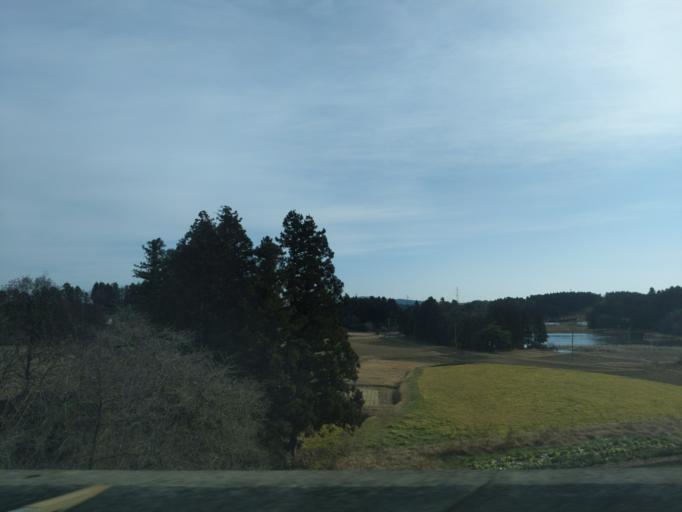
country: JP
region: Miyagi
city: Furukawa
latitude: 38.6354
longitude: 141.0075
